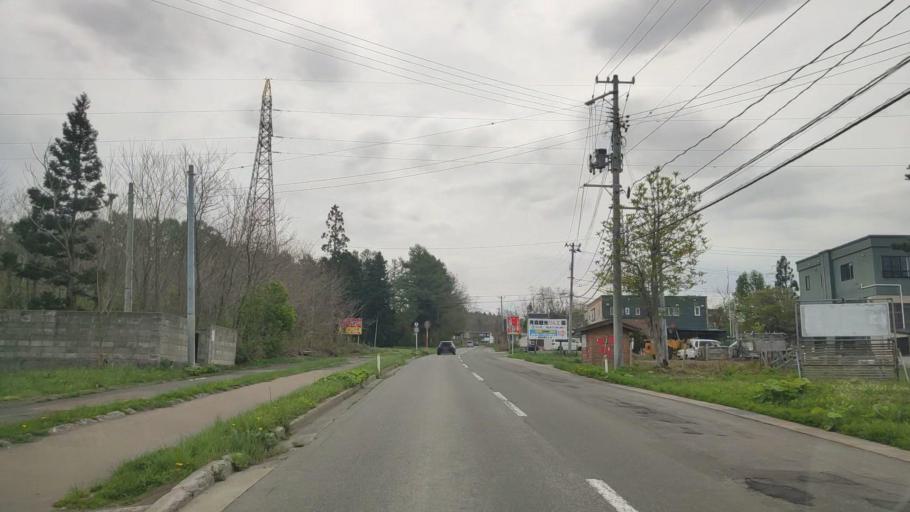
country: JP
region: Aomori
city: Aomori Shi
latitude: 40.7692
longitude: 140.7997
